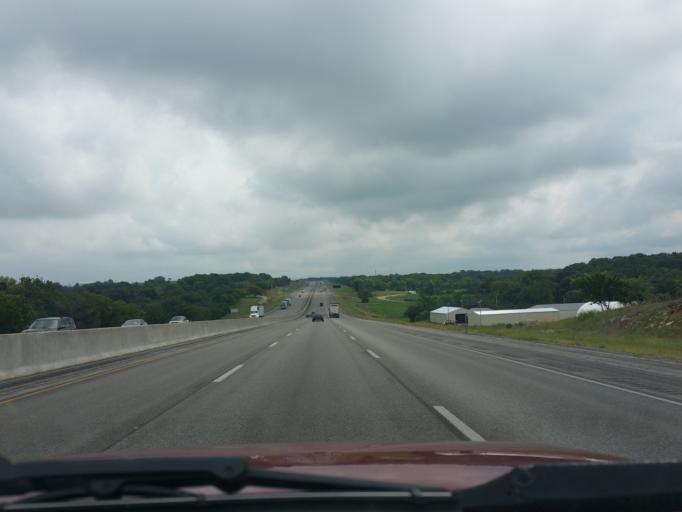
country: US
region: Kansas
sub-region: Shawnee County
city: Topeka
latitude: 39.0251
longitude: -95.5505
